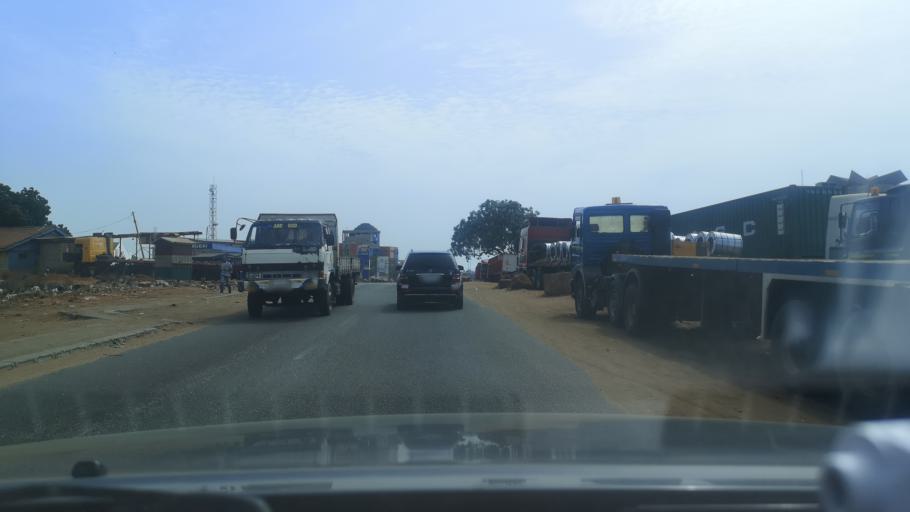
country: GH
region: Greater Accra
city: Tema
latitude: 5.6348
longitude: -0.0004
